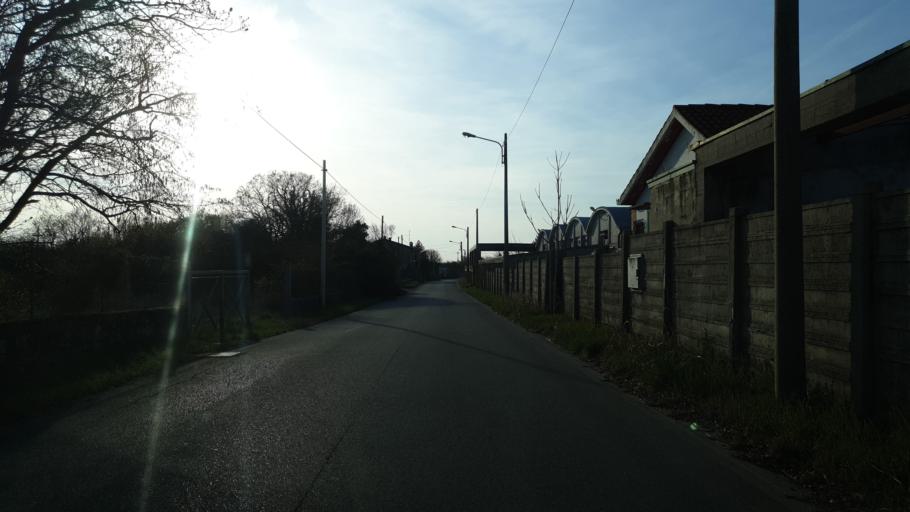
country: IT
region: Friuli Venezia Giulia
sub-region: Provincia di Trieste
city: Prosecco-Contovello
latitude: 45.7158
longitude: 13.7521
